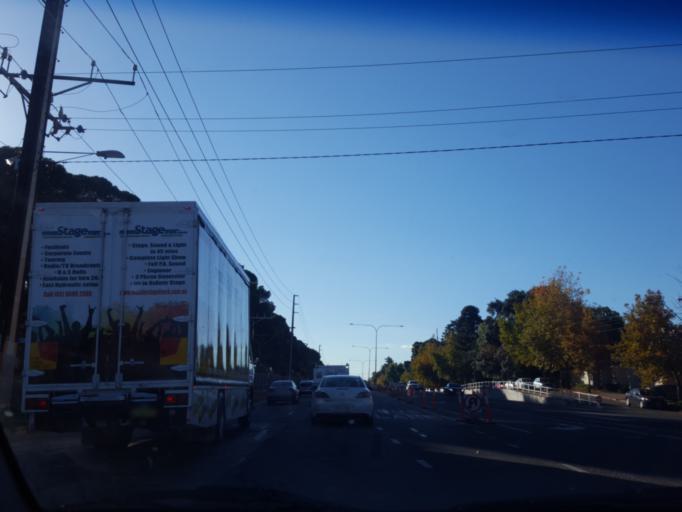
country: AU
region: South Australia
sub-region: Adelaide
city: Adelaide
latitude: -34.9162
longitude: 138.6141
